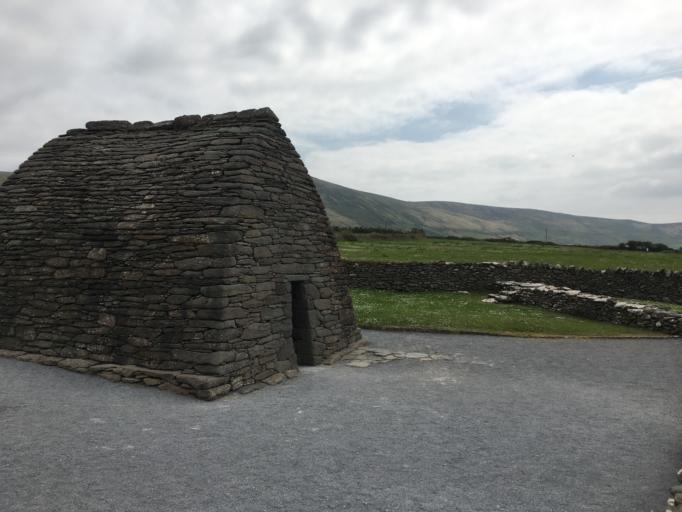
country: IE
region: Munster
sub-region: Ciarrai
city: Dingle
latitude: 52.1729
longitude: -10.3494
